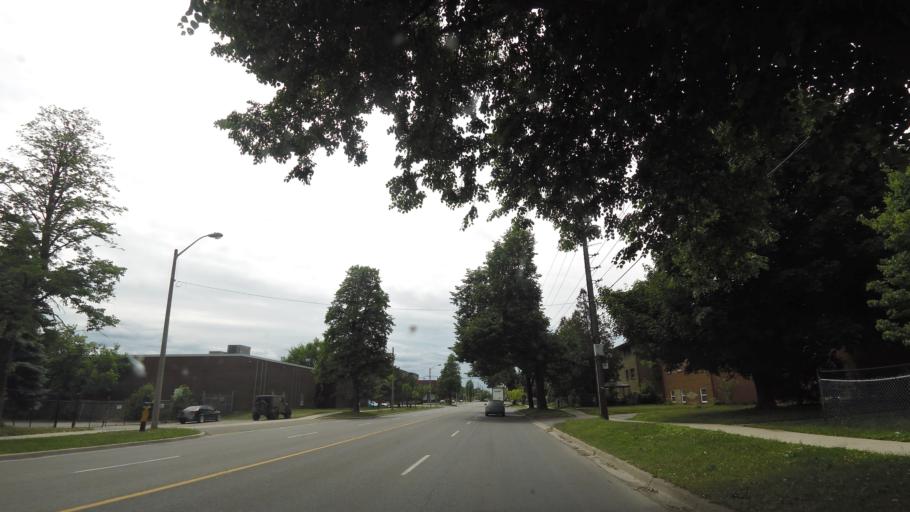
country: CA
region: Ontario
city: Etobicoke
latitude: 43.6027
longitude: -79.5409
